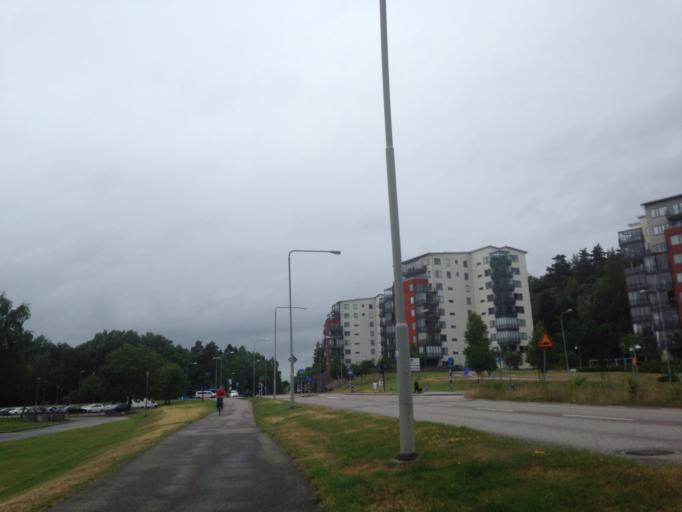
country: SE
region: Vaestra Goetaland
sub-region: Partille Kommun
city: Partille
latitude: 57.7207
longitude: 12.0600
